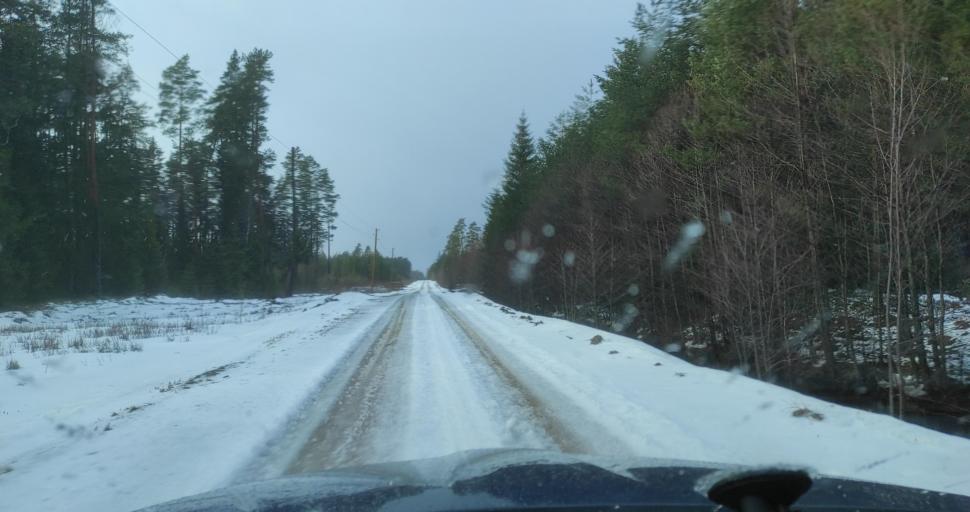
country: LV
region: Dundaga
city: Dundaga
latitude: 57.3812
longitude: 22.1552
